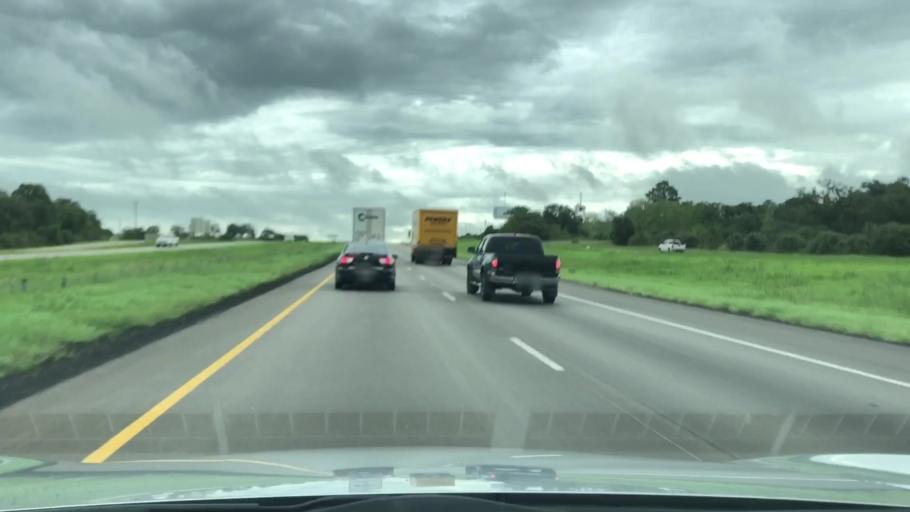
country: US
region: Texas
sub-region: Caldwell County
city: Luling
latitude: 29.6540
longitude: -97.5746
